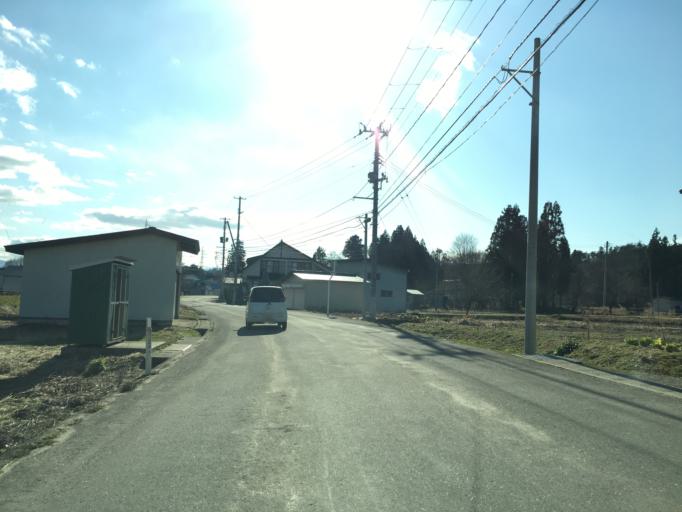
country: JP
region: Yamagata
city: Nagai
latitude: 37.9997
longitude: 140.0165
